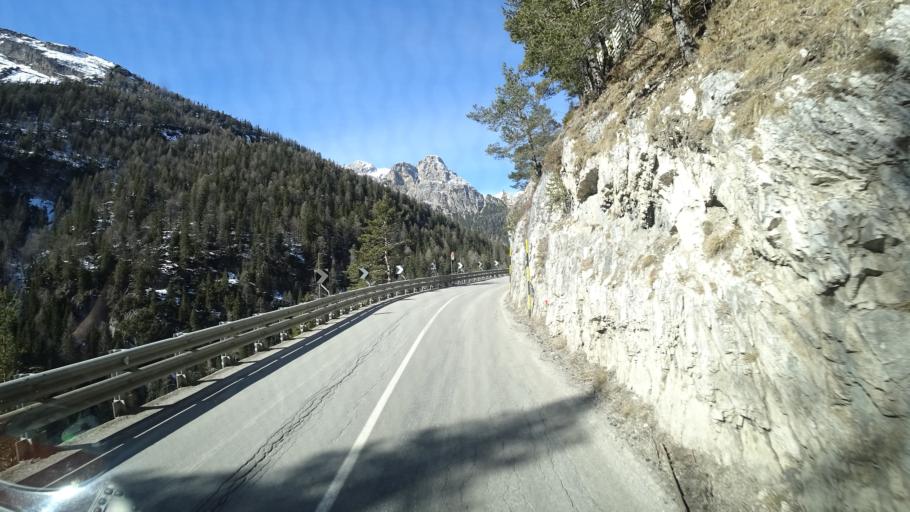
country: IT
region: Veneto
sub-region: Provincia di Belluno
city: Cortina d'Ampezzo
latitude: 46.5971
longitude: 12.1129
